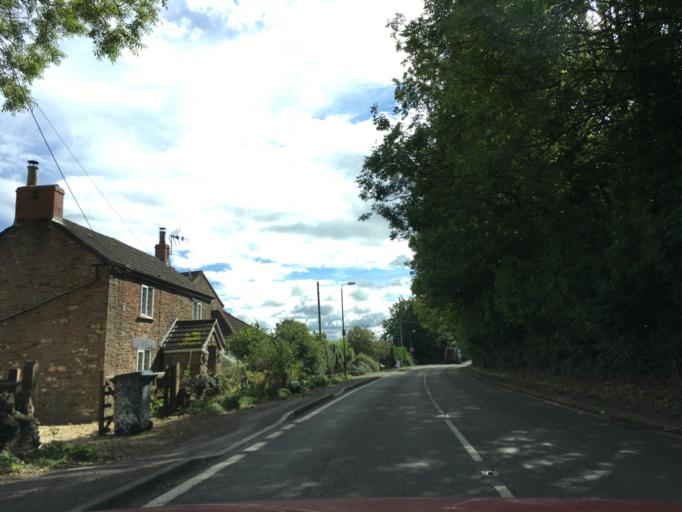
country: GB
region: England
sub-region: South Gloucestershire
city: Yate
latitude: 51.5695
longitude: -2.4465
